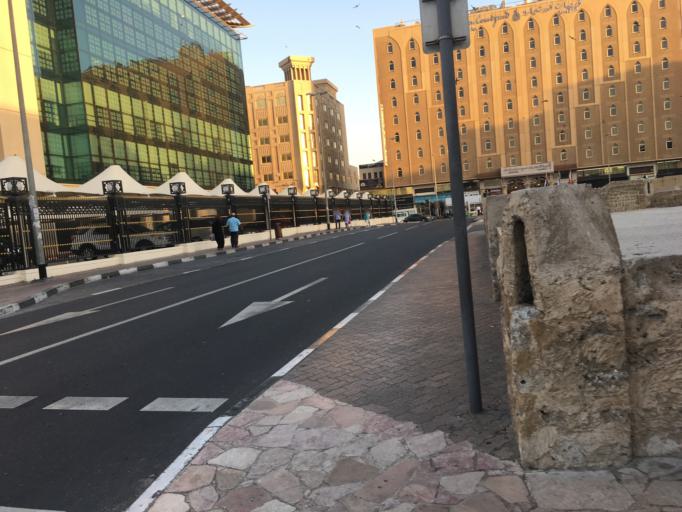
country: AE
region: Ash Shariqah
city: Sharjah
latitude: 25.2635
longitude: 55.2973
